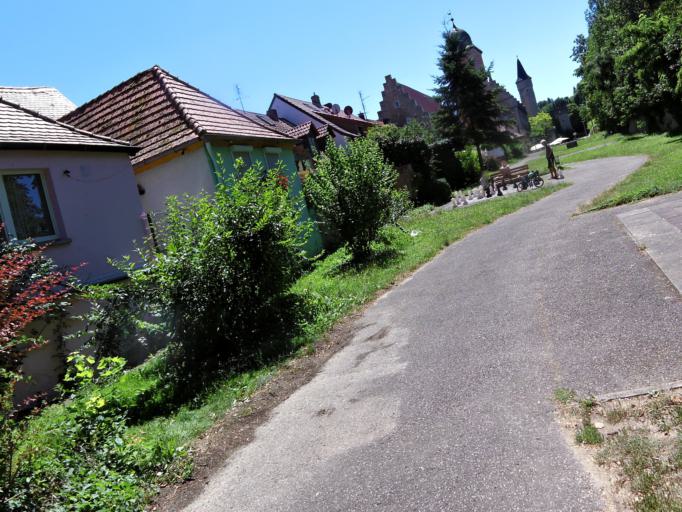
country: DE
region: Bavaria
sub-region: Regierungsbezirk Unterfranken
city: Ochsenfurt
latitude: 49.6658
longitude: 10.0616
